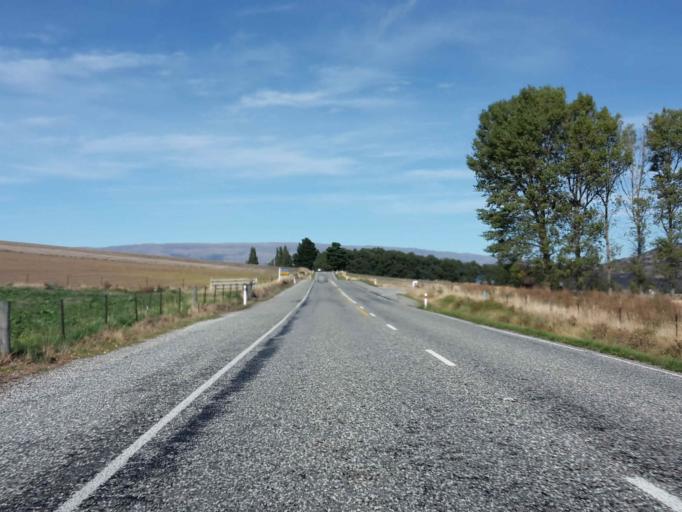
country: NZ
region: Otago
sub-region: Queenstown-Lakes District
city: Wanaka
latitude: -44.7659
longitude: 169.3491
